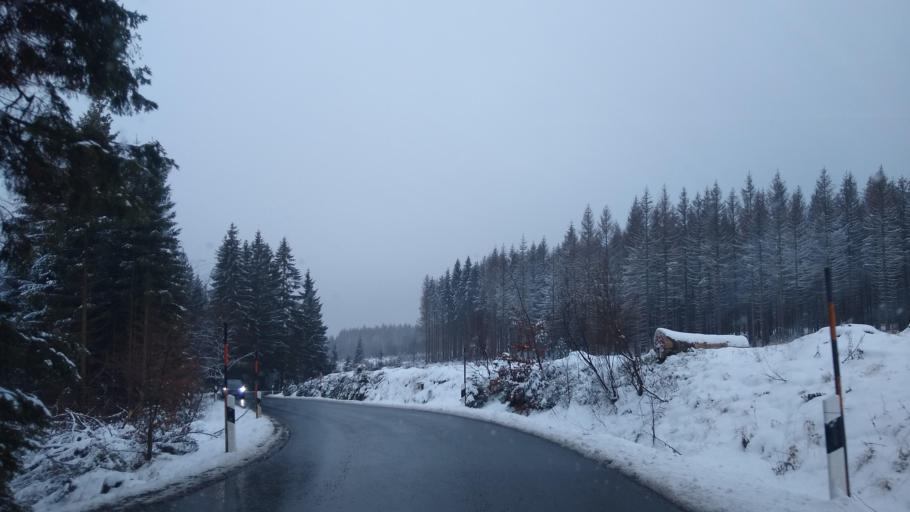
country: DE
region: Lower Saxony
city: Braunlage
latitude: 51.7492
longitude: 10.6309
